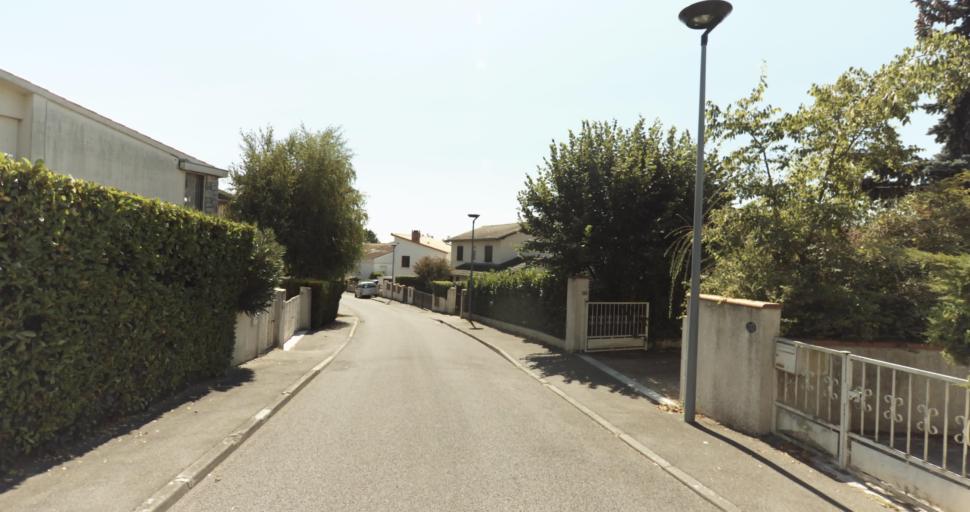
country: FR
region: Midi-Pyrenees
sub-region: Departement de la Haute-Garonne
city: L'Union
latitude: 43.6550
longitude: 1.4858
